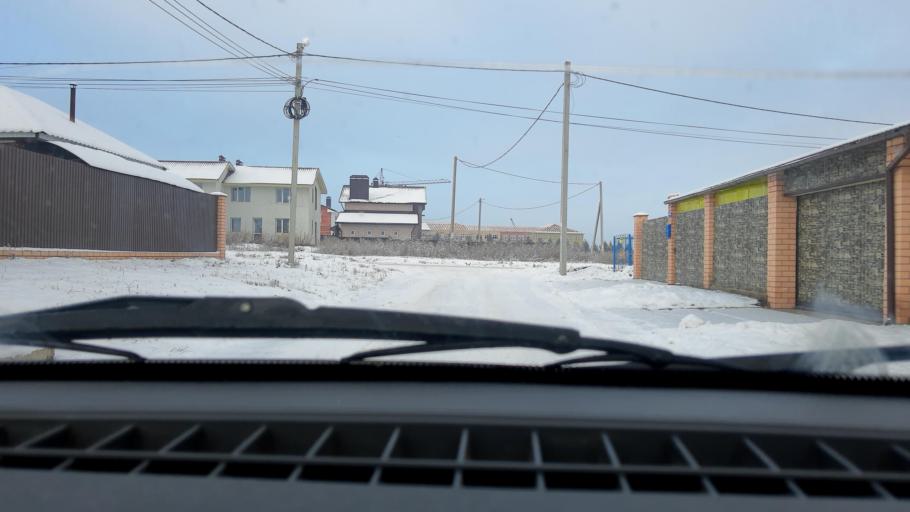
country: RU
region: Bashkortostan
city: Avdon
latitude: 54.4818
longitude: 55.8792
